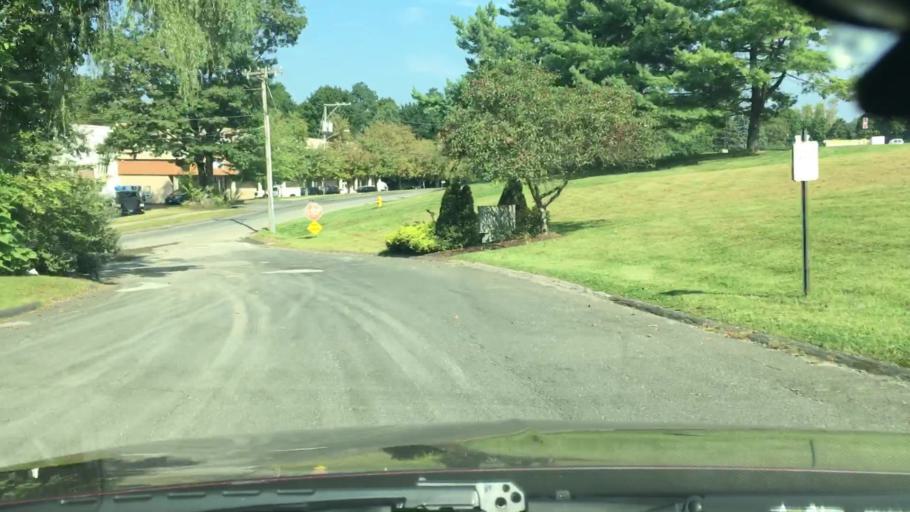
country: US
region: Connecticut
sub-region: Fairfield County
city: Bethel
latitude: 41.4094
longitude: -73.4066
